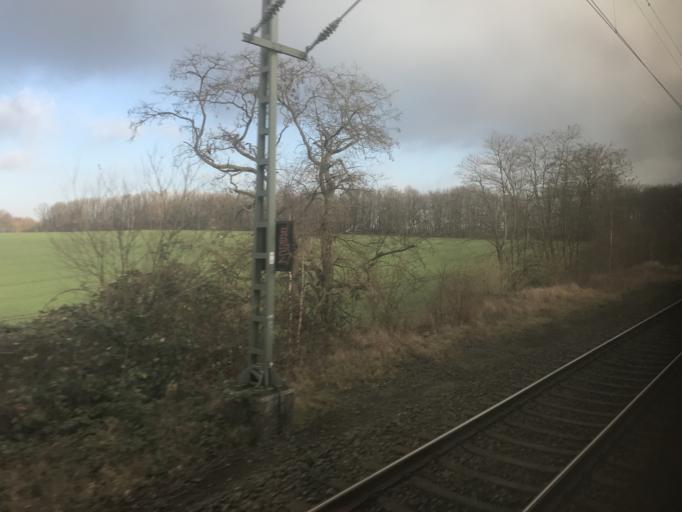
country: DE
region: North Rhine-Westphalia
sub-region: Regierungsbezirk Arnsberg
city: Bochum
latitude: 51.4868
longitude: 7.2746
